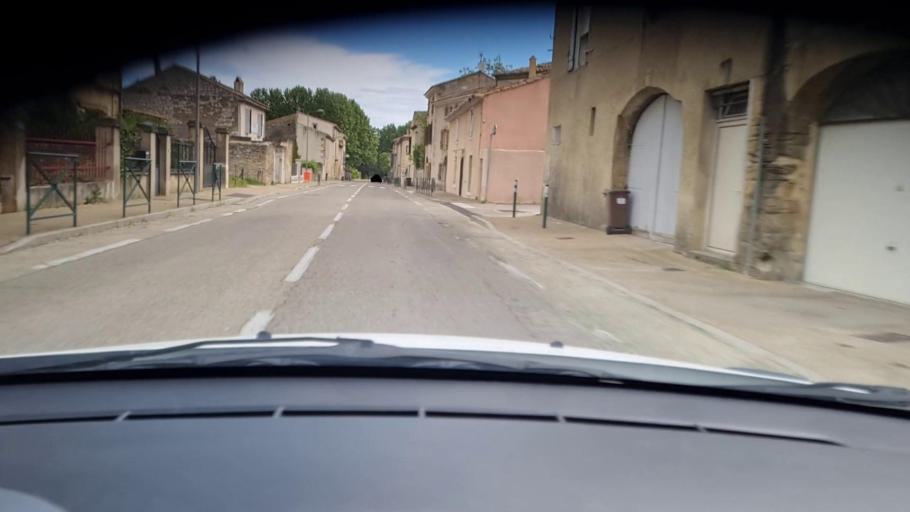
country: FR
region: Languedoc-Roussillon
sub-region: Departement du Gard
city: Sernhac
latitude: 43.9263
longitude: 4.5442
